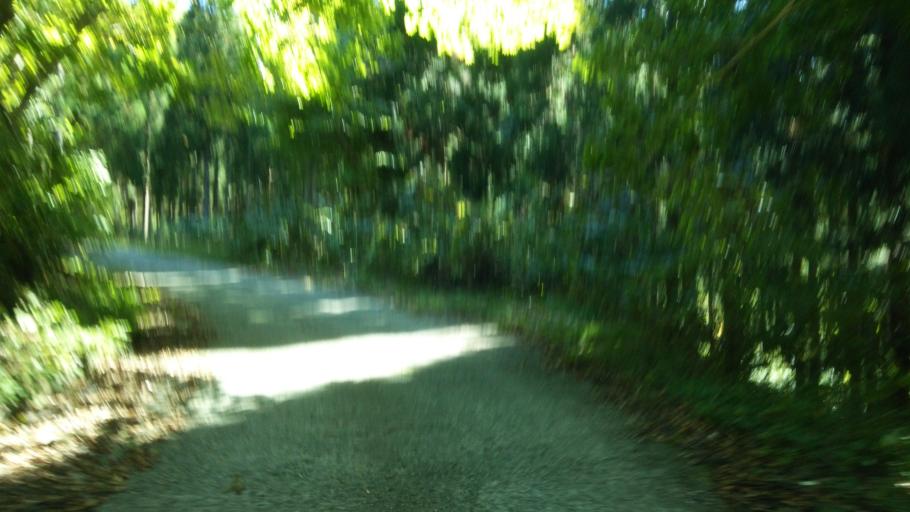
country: JP
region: Fukushima
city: Kitakata
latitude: 37.6200
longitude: 139.9808
